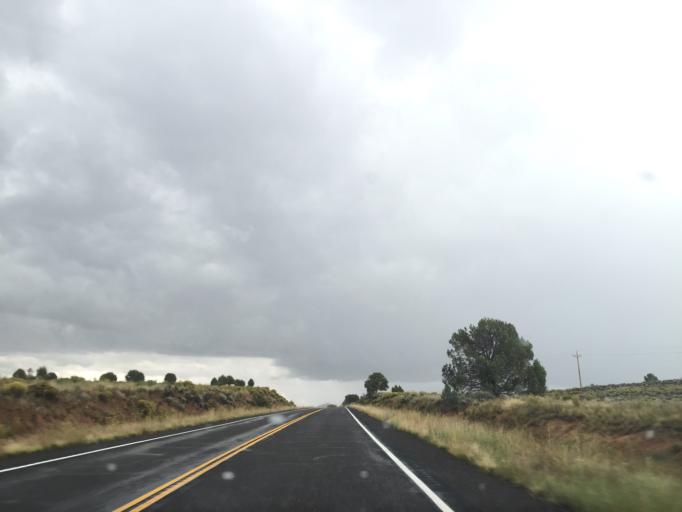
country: US
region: Utah
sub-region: Kane County
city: Kanab
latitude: 37.2294
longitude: -112.7294
